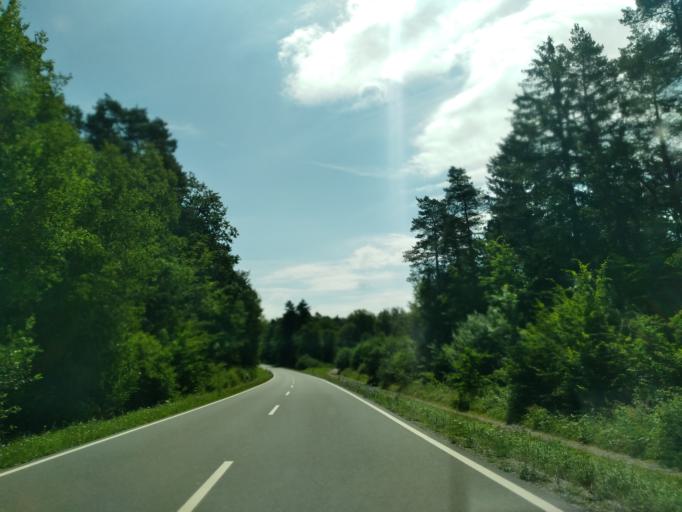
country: DE
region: Baden-Wuerttemberg
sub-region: Karlsruhe Region
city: Limbach
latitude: 49.4974
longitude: 9.2512
